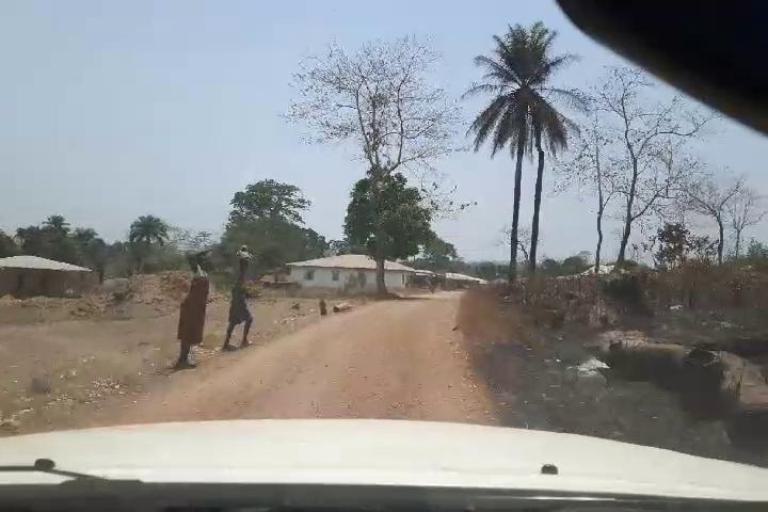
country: SL
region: Northern Province
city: Alikalia
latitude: 9.0636
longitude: -11.4857
